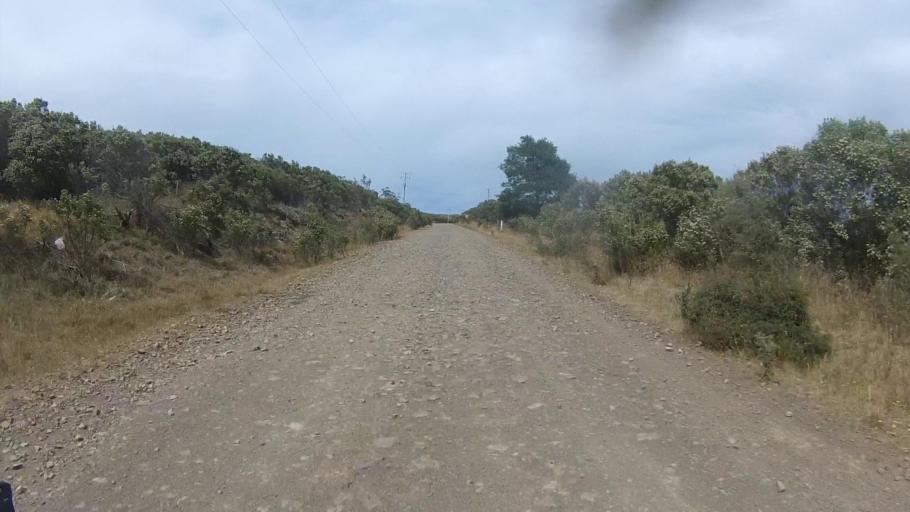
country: AU
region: Tasmania
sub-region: Sorell
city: Sorell
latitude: -42.7754
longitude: 147.8285
